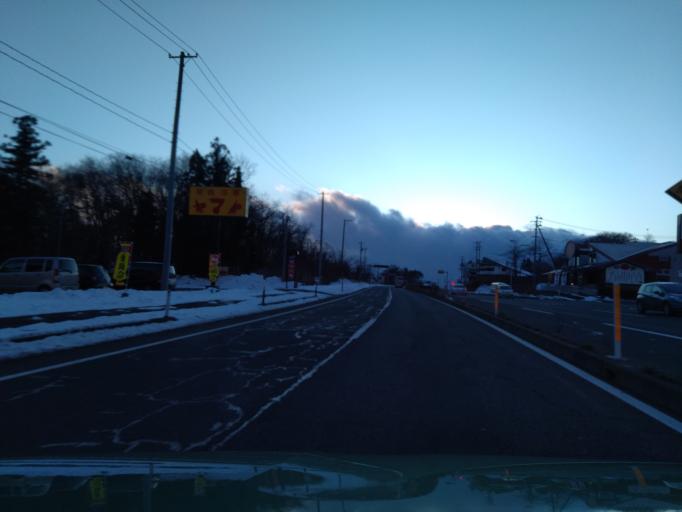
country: JP
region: Iwate
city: Shizukuishi
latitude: 39.7010
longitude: 141.0291
